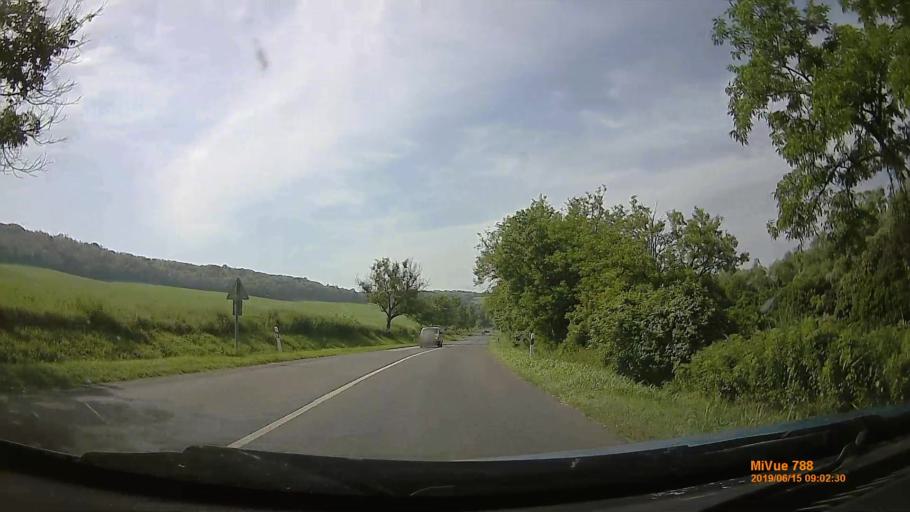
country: HU
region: Tolna
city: Iregszemcse
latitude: 46.7561
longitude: 18.1638
